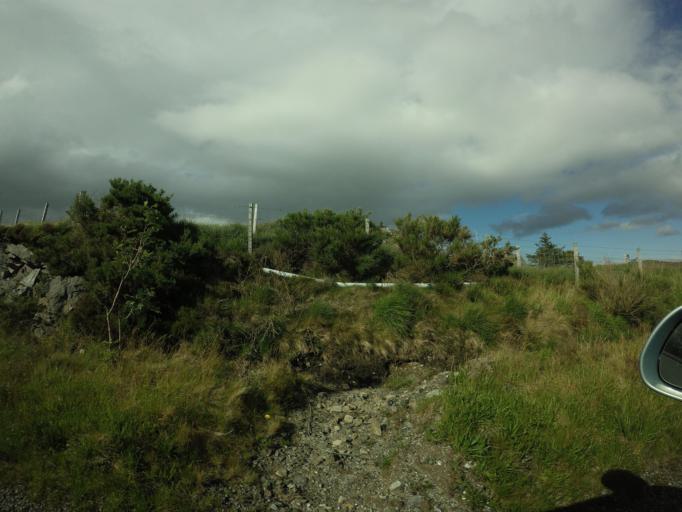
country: GB
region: Scotland
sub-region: Eilean Siar
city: Harris
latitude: 58.1928
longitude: -6.7118
